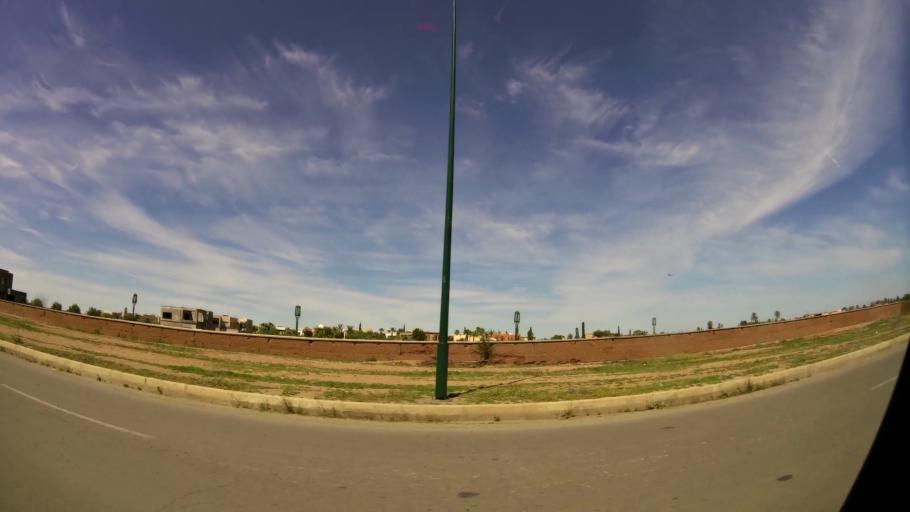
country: MA
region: Marrakech-Tensift-Al Haouz
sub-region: Marrakech
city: Marrakesh
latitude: 31.6130
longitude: -7.9466
